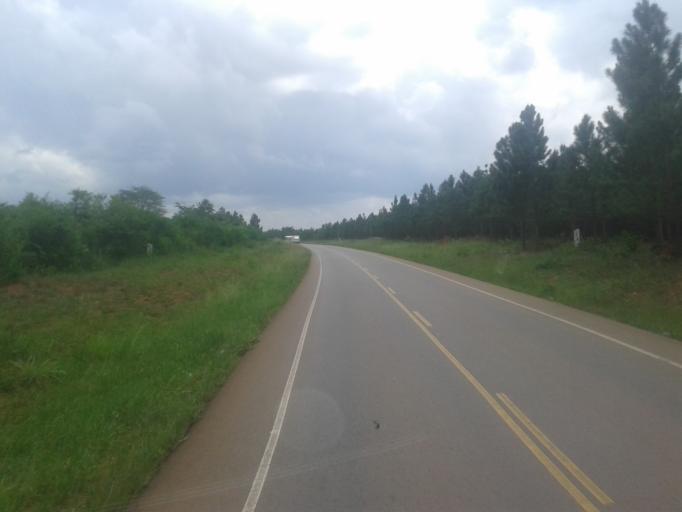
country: UG
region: Central Region
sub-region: Nakasongola District
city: Nakasongola
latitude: 1.2147
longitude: 32.4647
